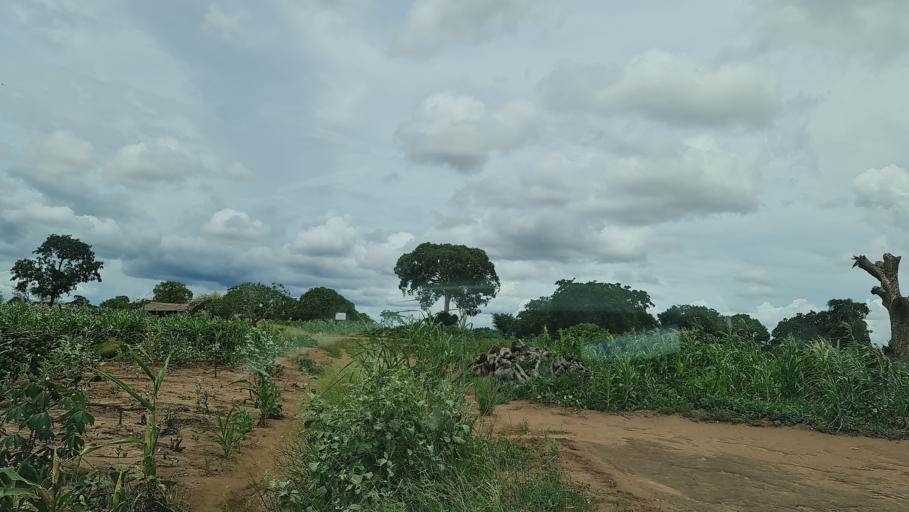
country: MZ
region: Nampula
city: Nacala
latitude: -14.7811
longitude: 39.9853
